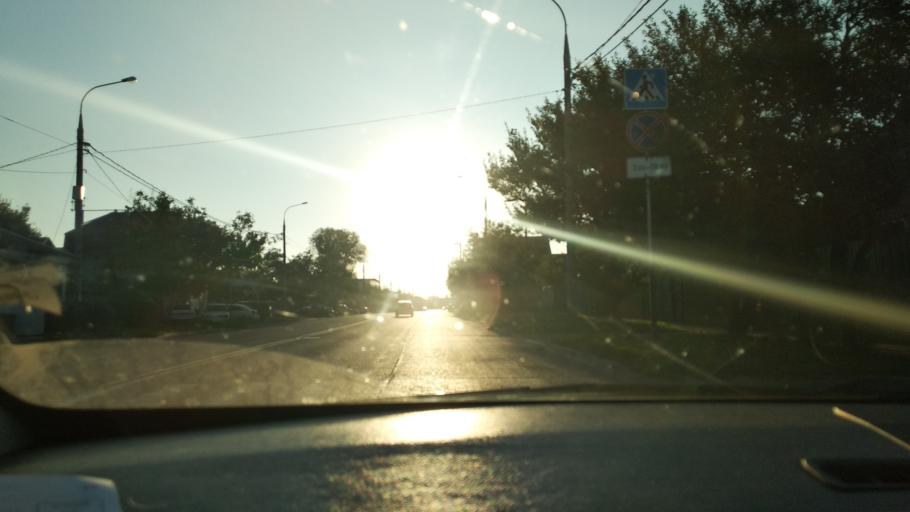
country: RU
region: Krasnodarskiy
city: Krasnodar
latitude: 45.0141
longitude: 39.0030
